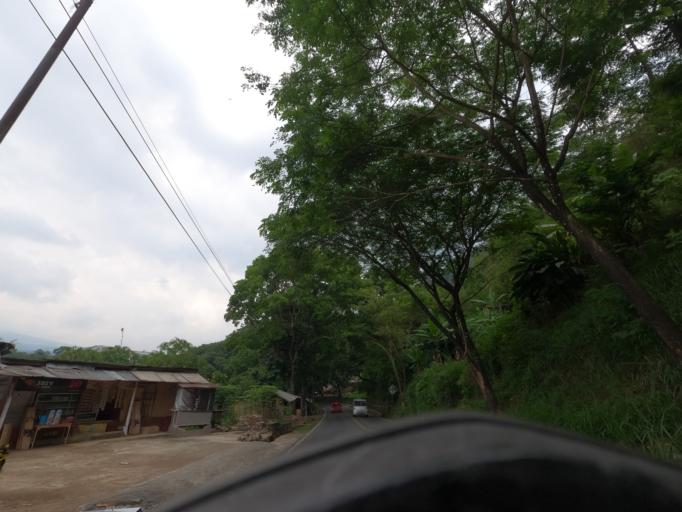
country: ID
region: West Java
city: Ciranjang-hilir
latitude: -6.7949
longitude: 107.0773
